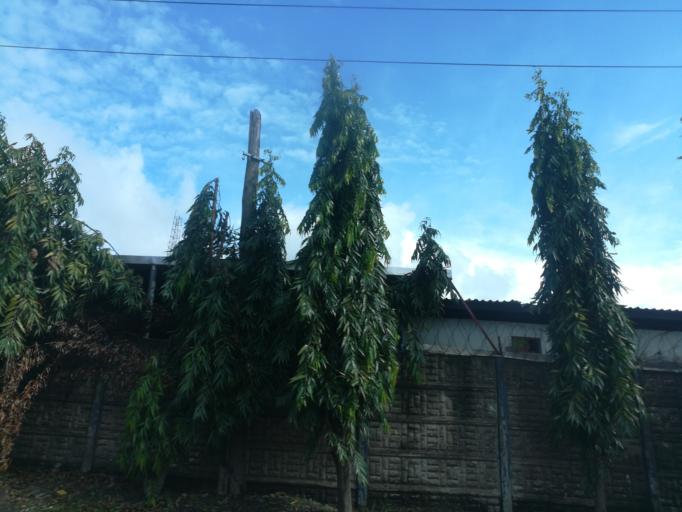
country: NG
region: Lagos
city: Agege
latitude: 6.6229
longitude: 3.3389
